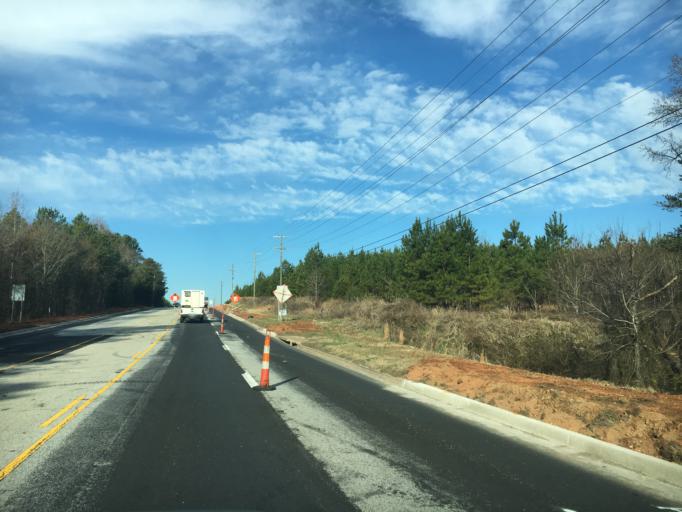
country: US
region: South Carolina
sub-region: Greenville County
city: Greer
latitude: 34.9058
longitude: -82.1960
